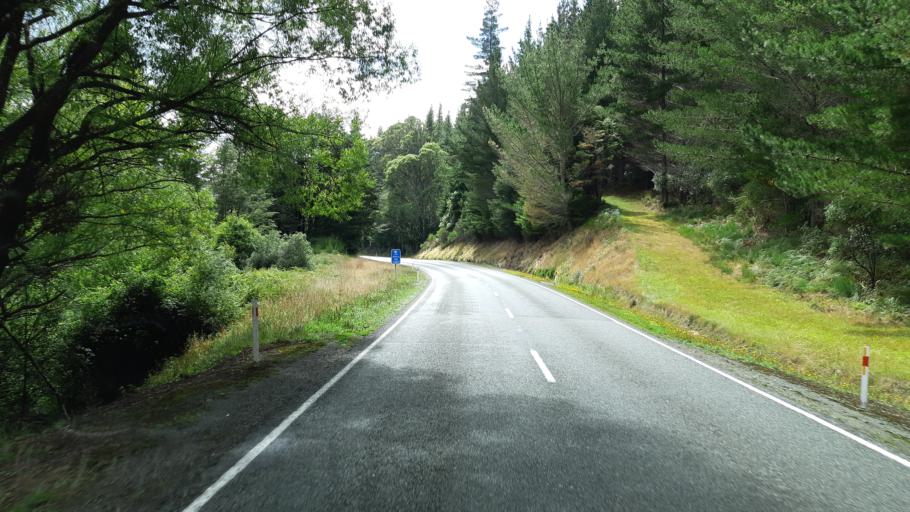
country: NZ
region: Tasman
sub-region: Tasman District
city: Wakefield
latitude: -41.5973
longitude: 172.7619
